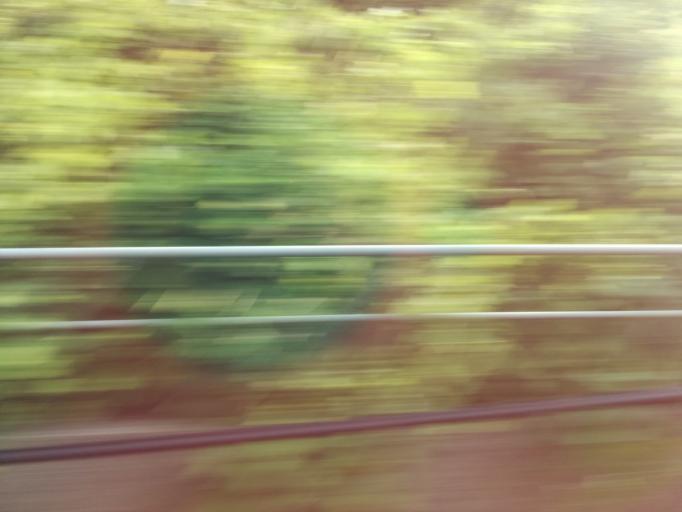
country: JP
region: Shizuoka
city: Kosai-shi
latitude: 34.6976
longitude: 137.5562
